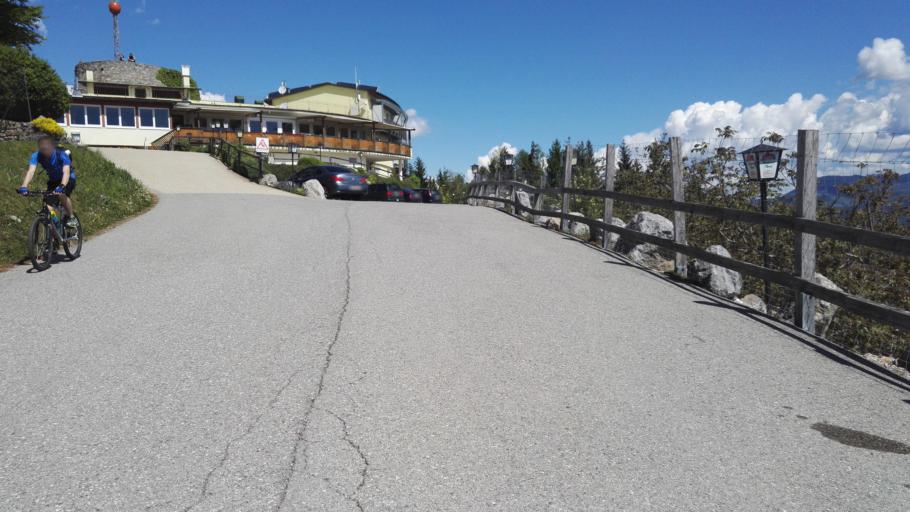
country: AT
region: Styria
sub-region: Graz Stadt
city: Goesting
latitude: 47.0898
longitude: 15.3857
